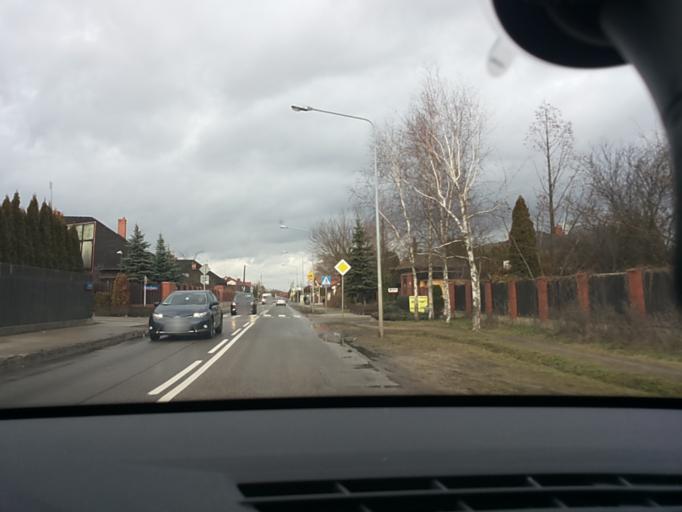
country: PL
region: Masovian Voivodeship
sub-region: Warszawa
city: Targowek
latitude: 52.3077
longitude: 21.0521
